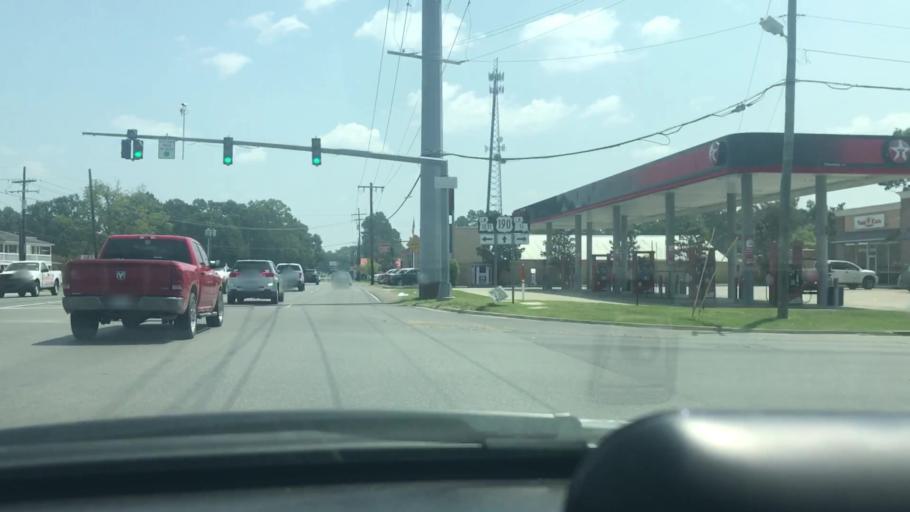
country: US
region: Louisiana
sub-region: Livingston Parish
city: Denham Springs
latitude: 30.4843
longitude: -90.9437
